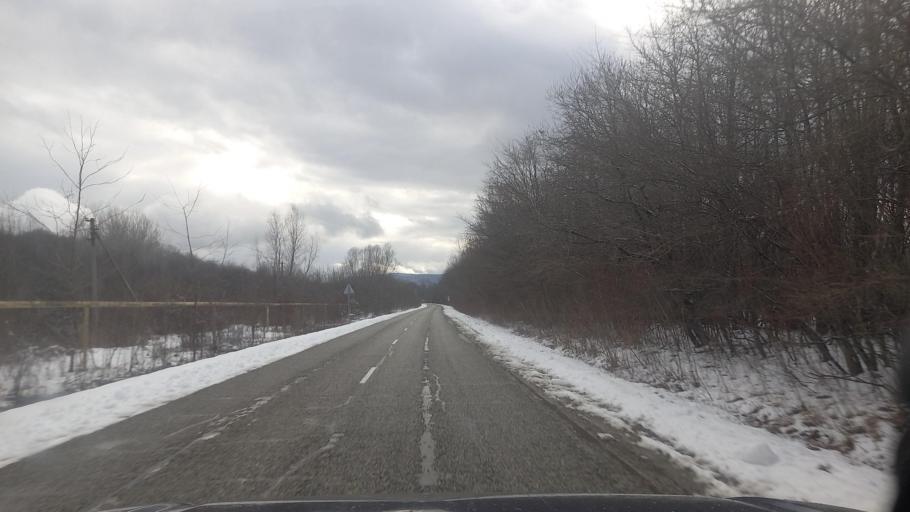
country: RU
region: Krasnodarskiy
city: Smolenskaya
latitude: 44.7446
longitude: 38.8390
